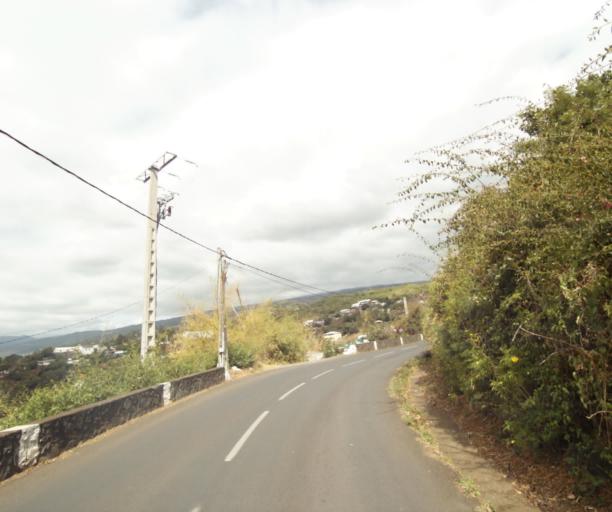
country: RE
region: Reunion
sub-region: Reunion
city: Saint-Paul
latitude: -21.0219
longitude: 55.2909
